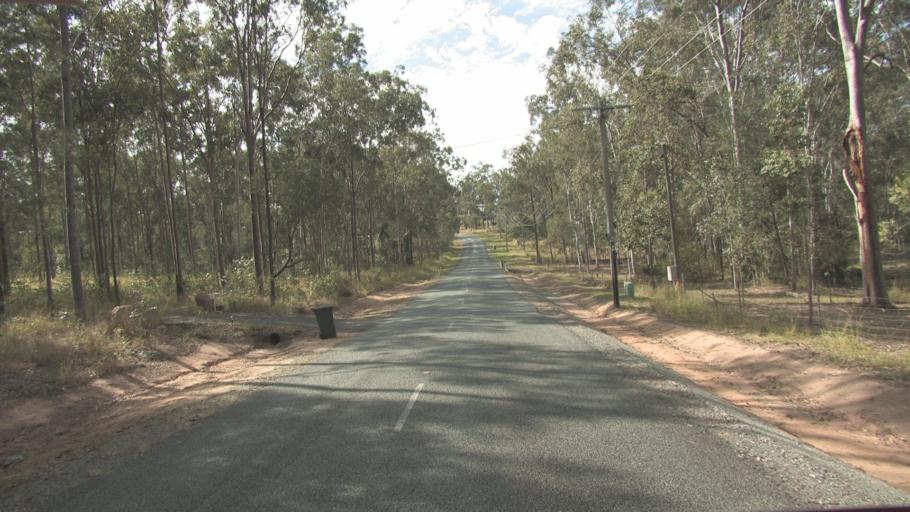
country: AU
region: Queensland
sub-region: Logan
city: North Maclean
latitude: -27.7401
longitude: 152.9770
